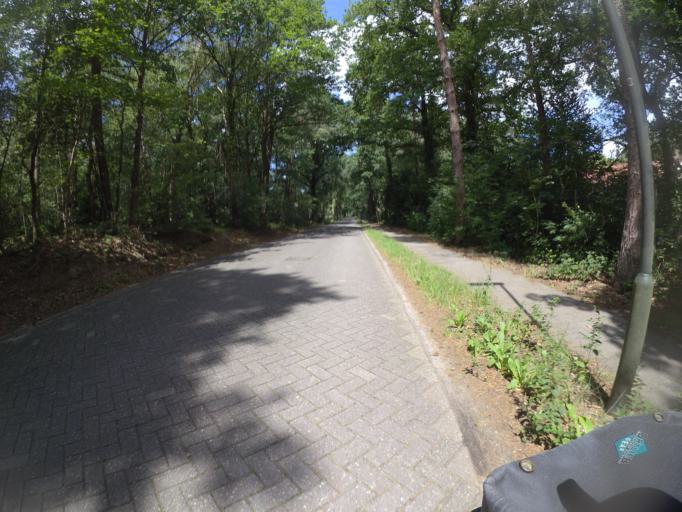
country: NL
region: North Brabant
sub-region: Gemeente Haaren
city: Haaren
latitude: 51.5751
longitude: 5.2258
